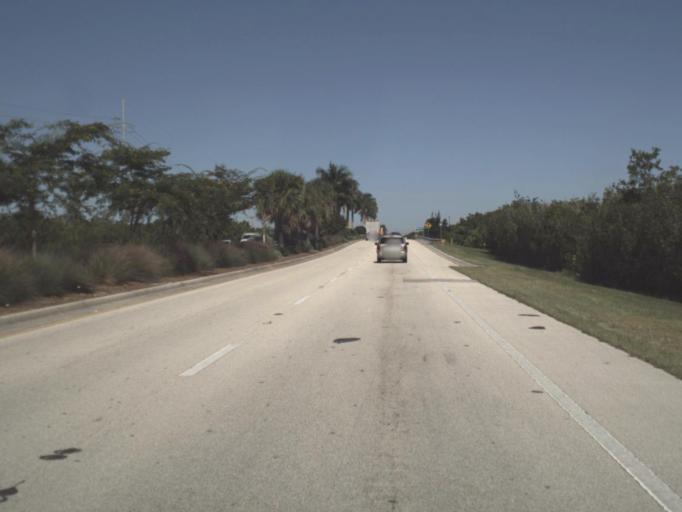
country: US
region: Florida
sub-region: Collier County
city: Marco
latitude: 25.9933
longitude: -81.7019
